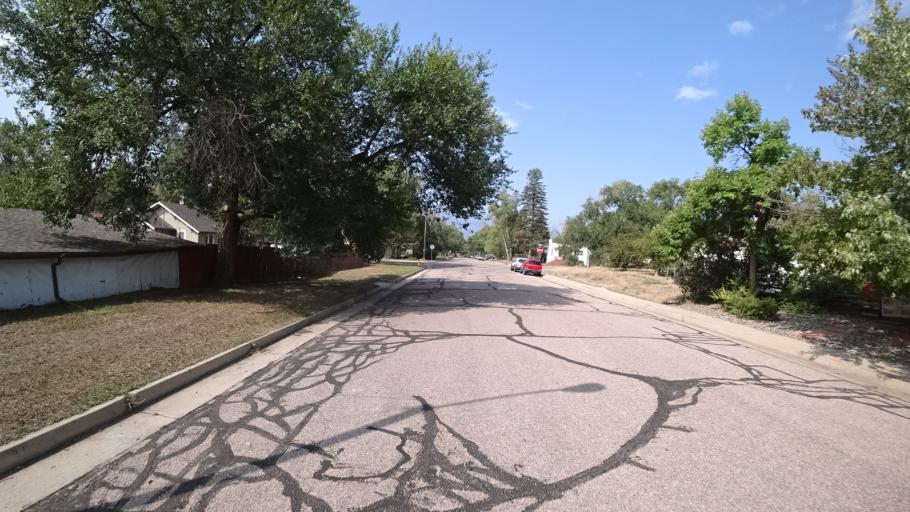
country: US
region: Colorado
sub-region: El Paso County
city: Colorado Springs
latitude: 38.8476
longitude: -104.7908
